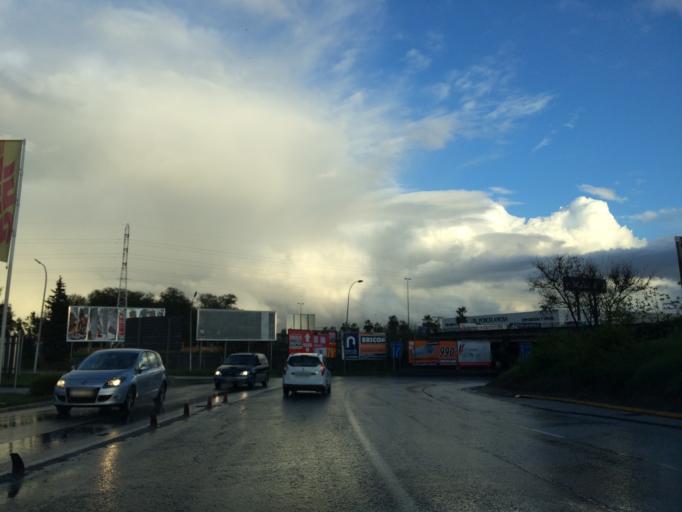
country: ES
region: Andalusia
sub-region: Provincia de Sevilla
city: Sevilla
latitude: 37.3869
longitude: -5.9353
